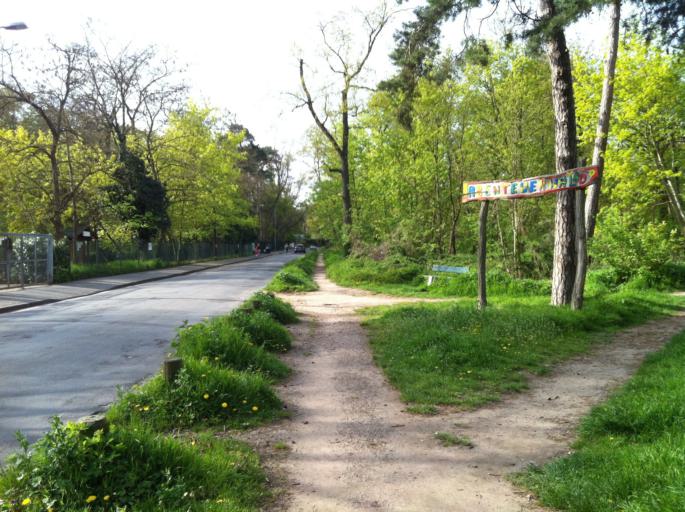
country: DE
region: Rheinland-Pfalz
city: Budenheim
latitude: 50.0067
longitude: 8.2037
